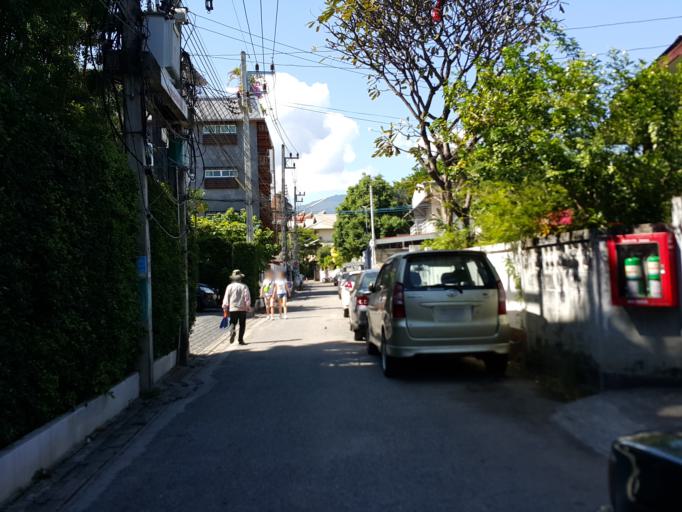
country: TH
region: Chiang Mai
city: Chiang Mai
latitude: 18.7865
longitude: 98.9900
